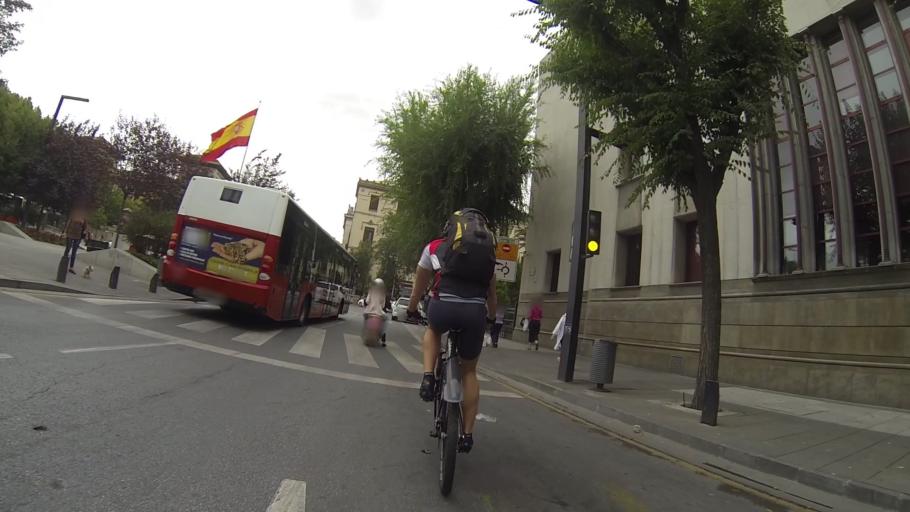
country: ES
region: Andalusia
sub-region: Provincia de Granada
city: Granada
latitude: 37.1831
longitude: -3.6027
